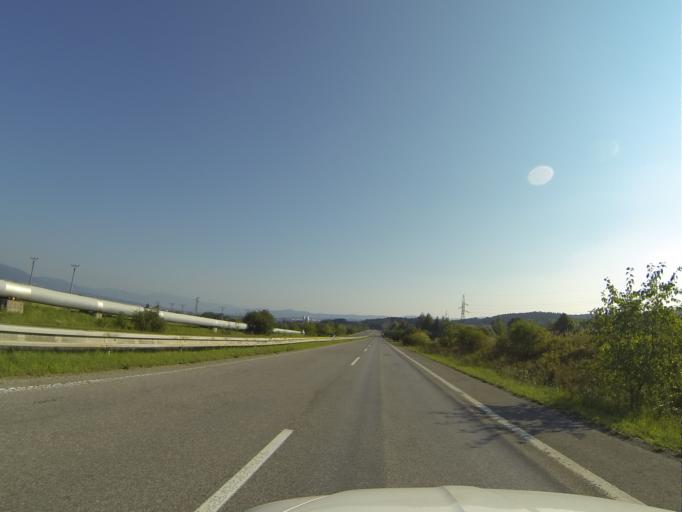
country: SK
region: Nitriansky
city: Prievidza
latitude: 48.7437
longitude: 18.6204
